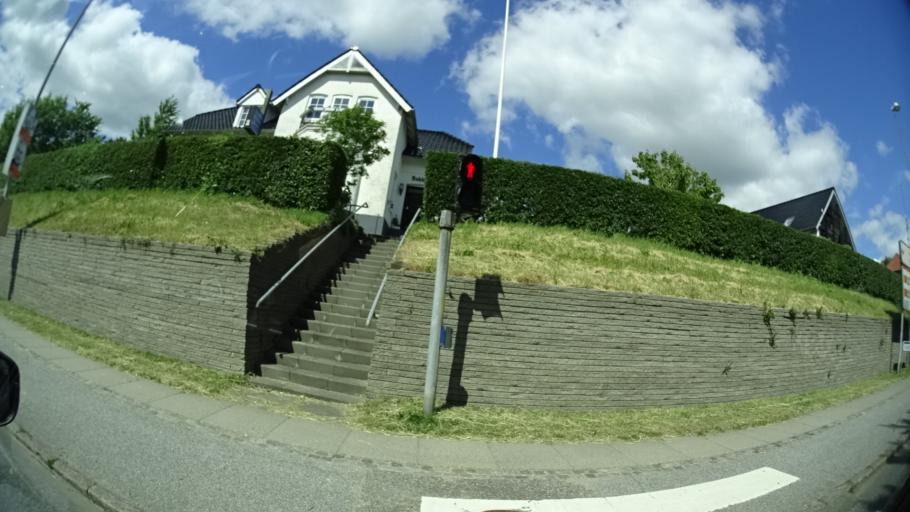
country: DK
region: Central Jutland
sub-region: Syddjurs Kommune
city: Ronde
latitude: 56.2995
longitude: 10.4816
